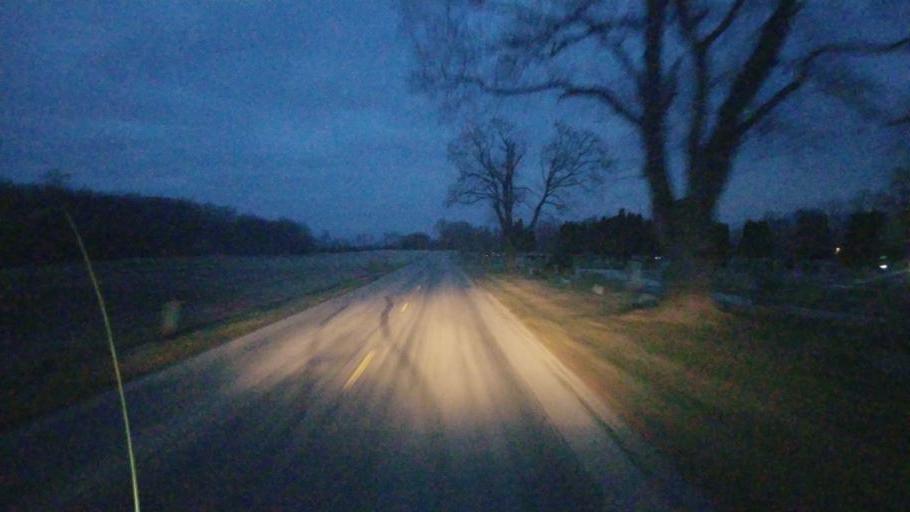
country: US
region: Ohio
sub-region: Marion County
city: Prospect
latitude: 40.4545
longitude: -83.1918
